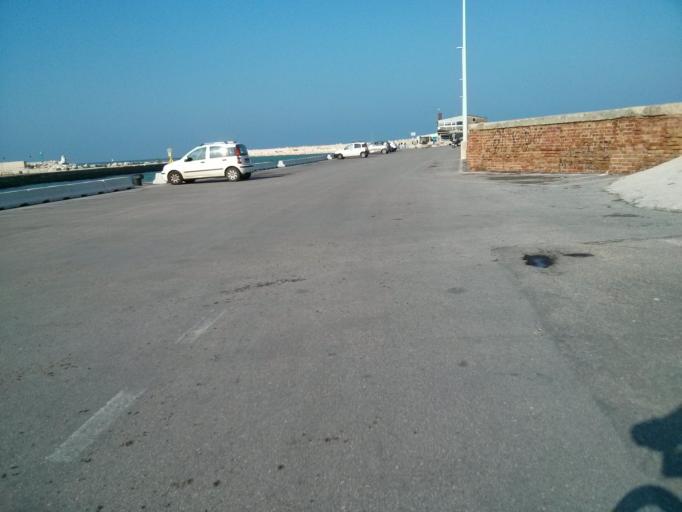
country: IT
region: The Marches
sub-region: Provincia di Pesaro e Urbino
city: Pesaro
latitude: 43.9235
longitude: 12.9065
